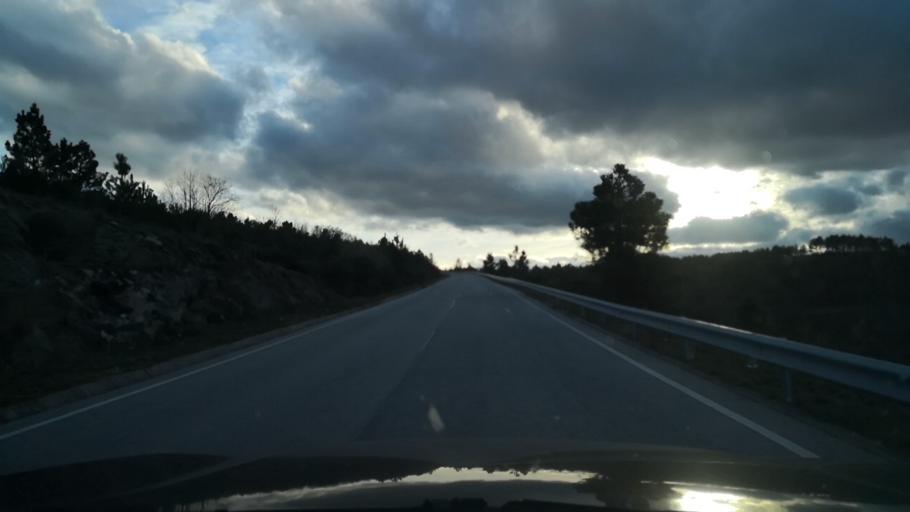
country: PT
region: Braganca
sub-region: Carrazeda de Ansiaes
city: Carrazeda de Anciaes
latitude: 41.2510
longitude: -7.3208
